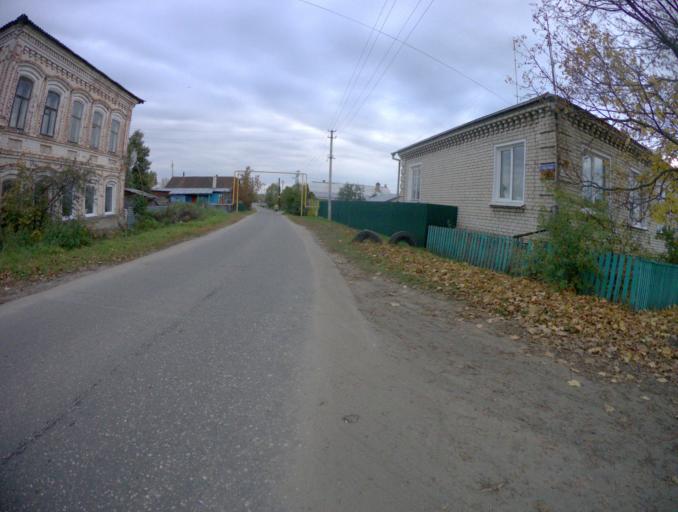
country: RU
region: Vladimir
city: Mstera
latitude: 56.3720
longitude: 41.9367
